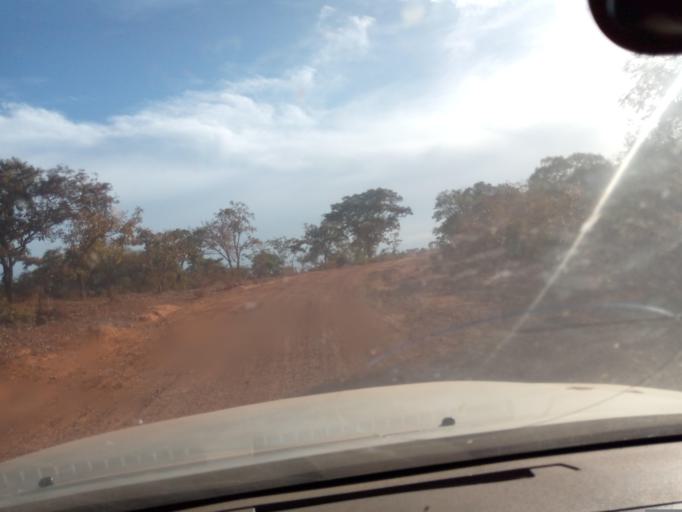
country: ML
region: Sikasso
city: Sikasso
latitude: 11.4133
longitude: -5.5692
